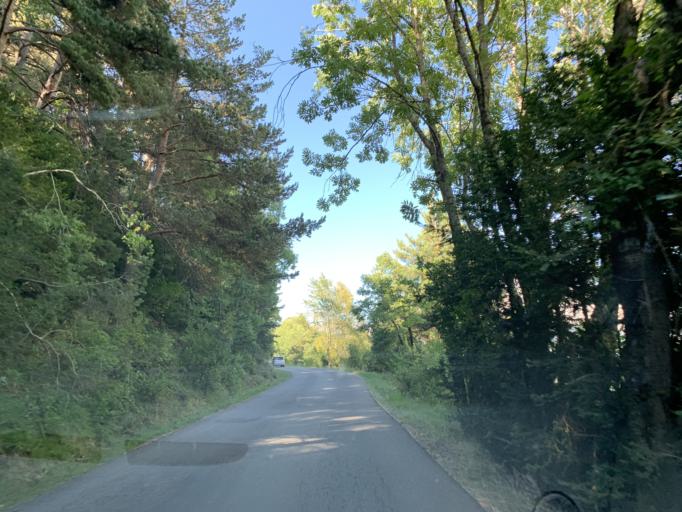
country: ES
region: Aragon
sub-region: Provincia de Huesca
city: Hoz de Jaca
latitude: 42.6929
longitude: -0.3320
